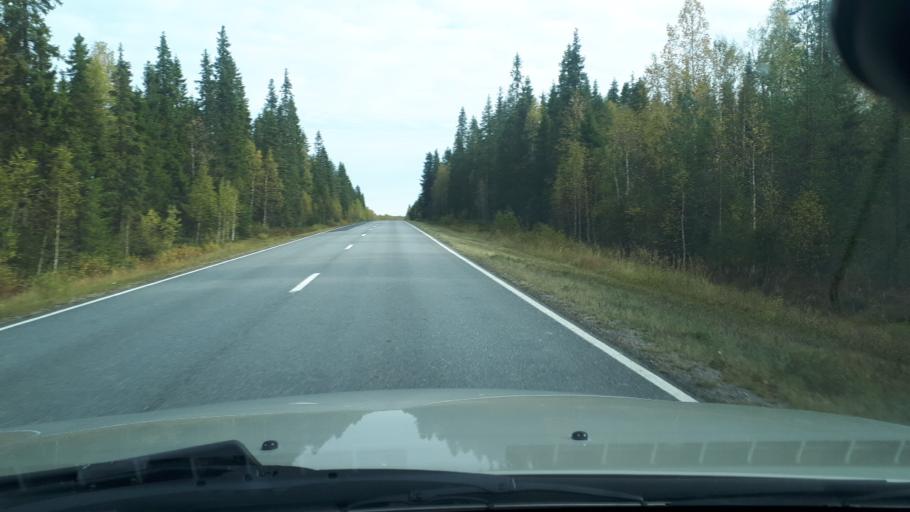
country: FI
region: Lapland
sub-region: Rovaniemi
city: Ranua
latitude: 65.9744
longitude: 26.1122
